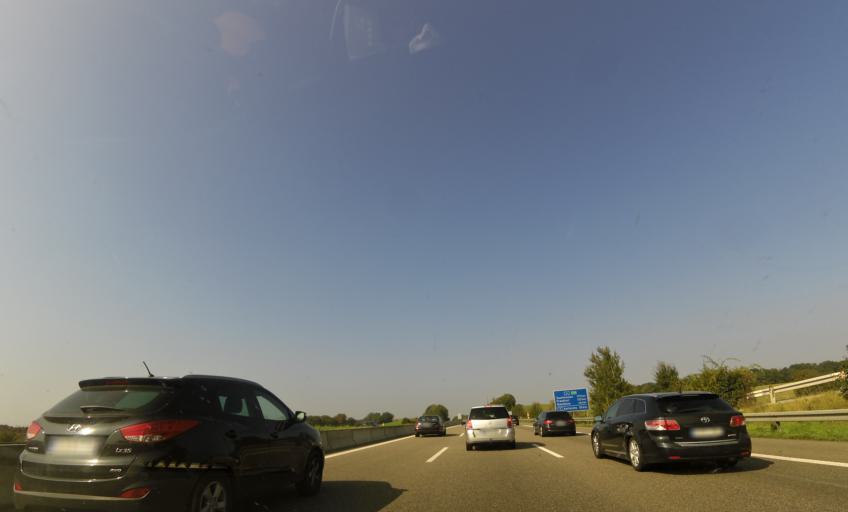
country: DE
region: Baden-Wuerttemberg
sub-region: Karlsruhe Region
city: Sinsheim
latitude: 49.2536
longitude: 8.8441
